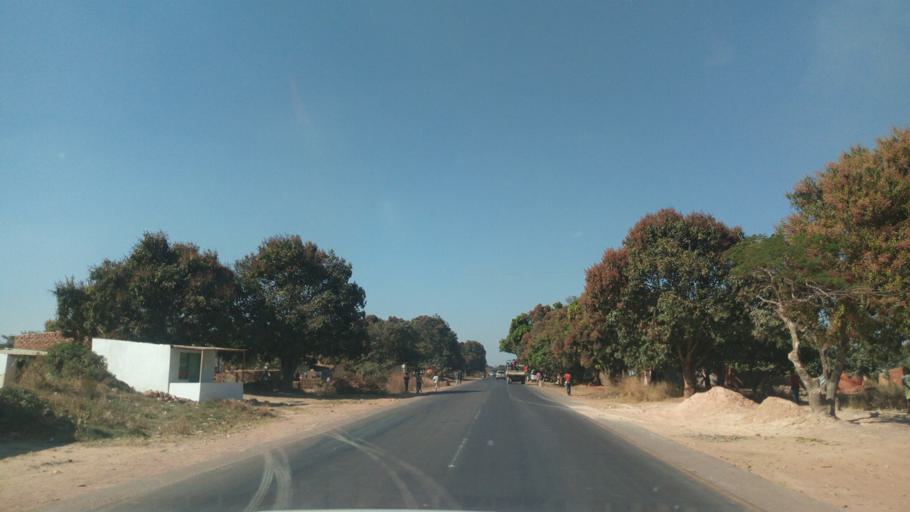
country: CD
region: Katanga
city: Lubumbashi
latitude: -11.5569
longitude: 27.5779
